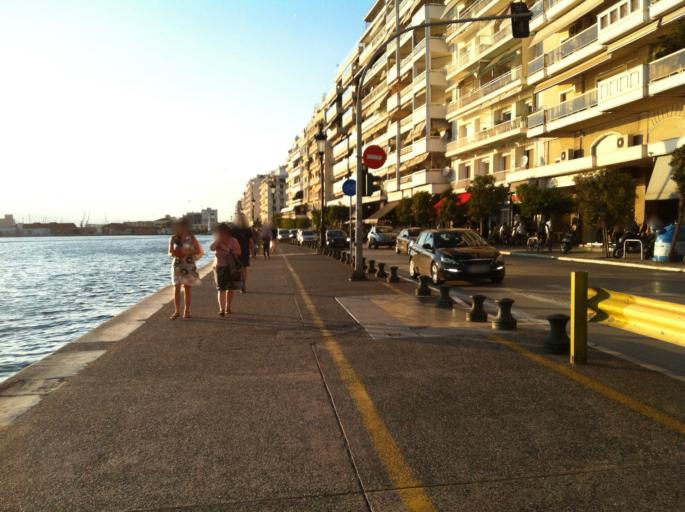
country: GR
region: Central Macedonia
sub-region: Nomos Thessalonikis
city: Thessaloniki
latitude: 40.6305
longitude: 22.9428
